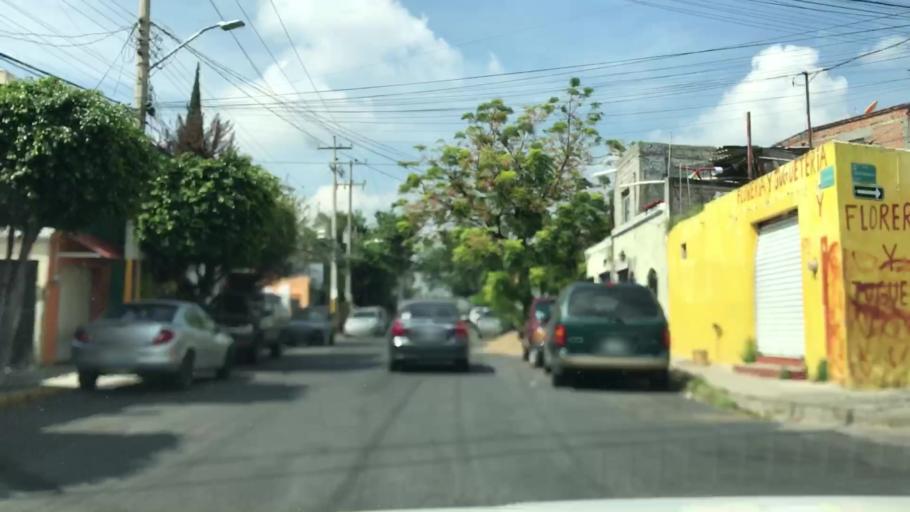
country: MX
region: Jalisco
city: Guadalajara
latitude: 20.6393
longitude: -103.4204
